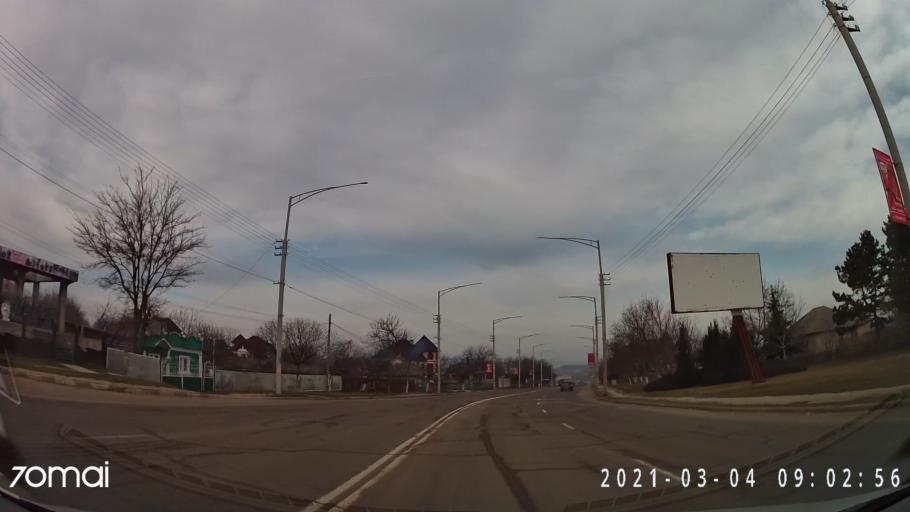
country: MD
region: Balti
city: Balti
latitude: 47.7455
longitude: 27.9494
